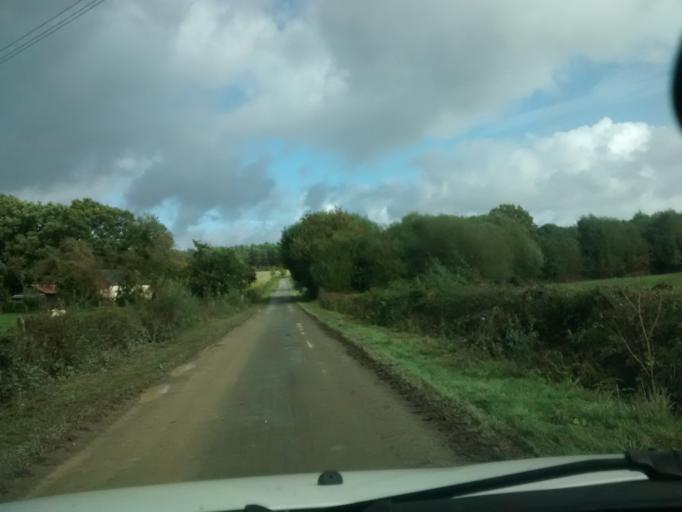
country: FR
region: Brittany
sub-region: Departement d'Ille-et-Vilaine
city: Chateaubourg
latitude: 48.1427
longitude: -1.4083
